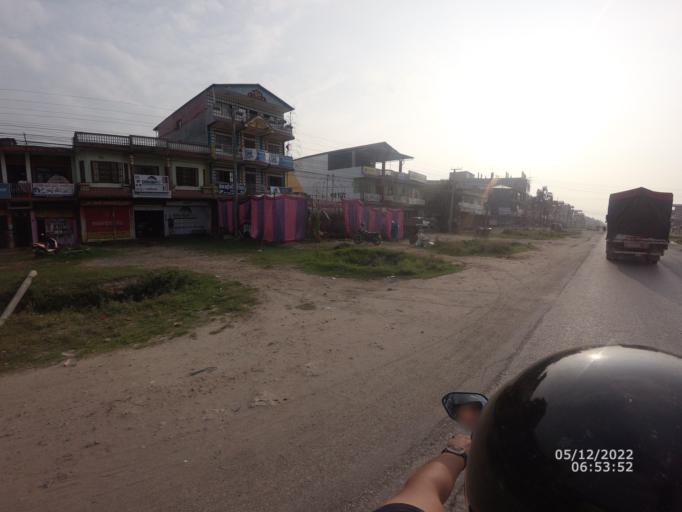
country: NP
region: Central Region
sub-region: Narayani Zone
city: Bharatpur
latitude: 27.7056
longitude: 84.3947
